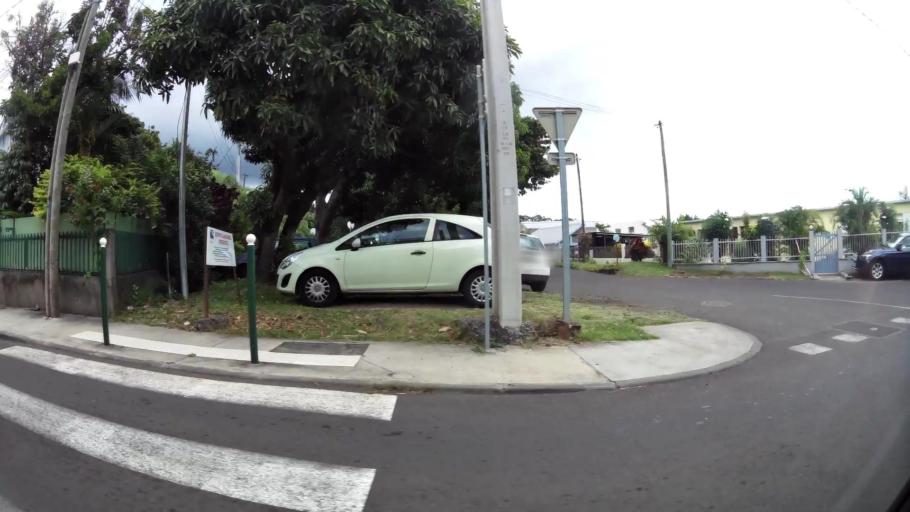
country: RE
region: Reunion
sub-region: Reunion
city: Saint-Denis
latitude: -20.8927
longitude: 55.4742
